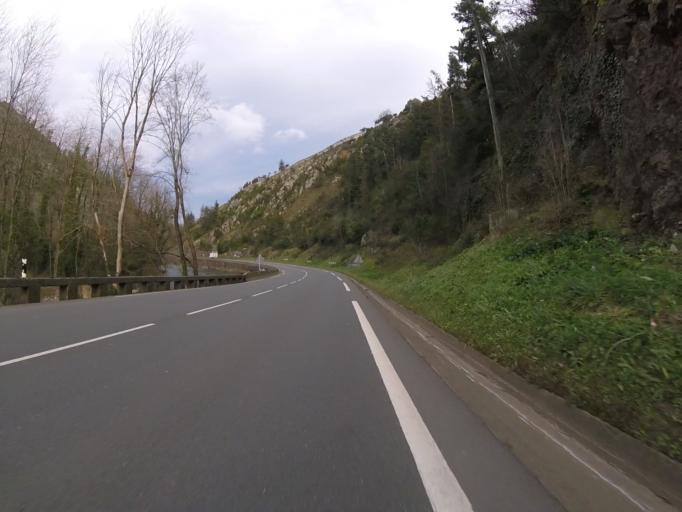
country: ES
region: Basque Country
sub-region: Provincia de Guipuzcoa
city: Cestona
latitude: 43.2436
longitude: -2.2584
